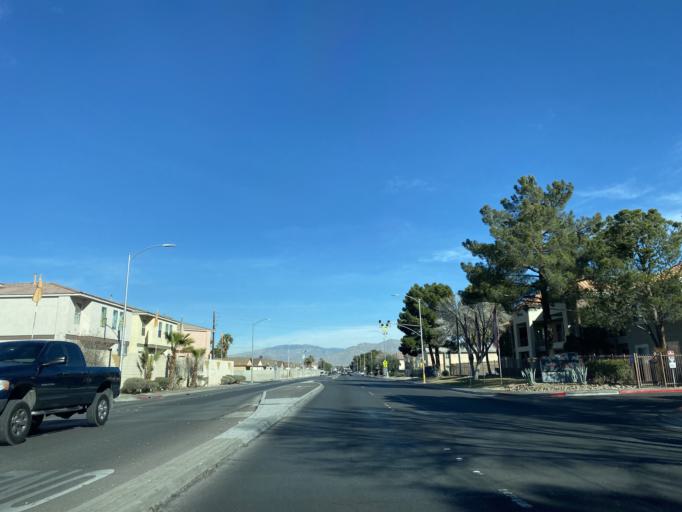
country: US
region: Nevada
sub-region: Clark County
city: Las Vegas
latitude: 36.1978
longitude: -115.2238
